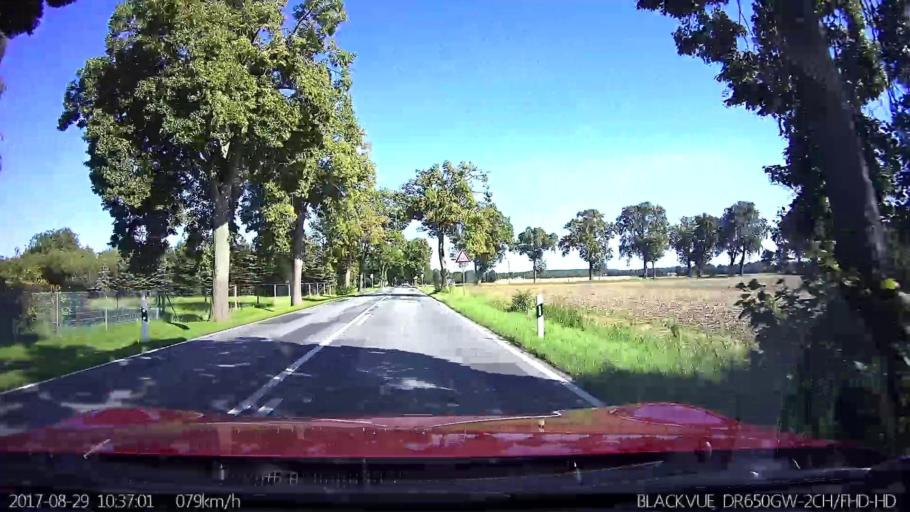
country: DE
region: Mecklenburg-Vorpommern
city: Tribsees
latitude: 54.1524
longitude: 12.8039
